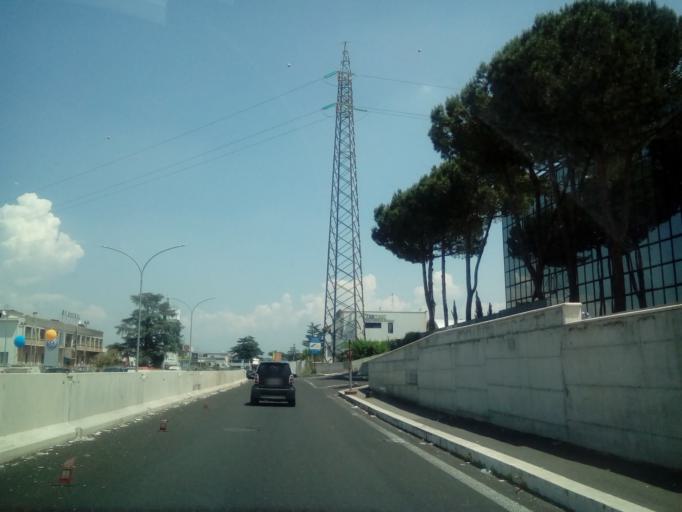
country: IT
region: Latium
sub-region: Citta metropolitana di Roma Capitale
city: Colle Verde
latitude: 41.9326
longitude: 12.5869
